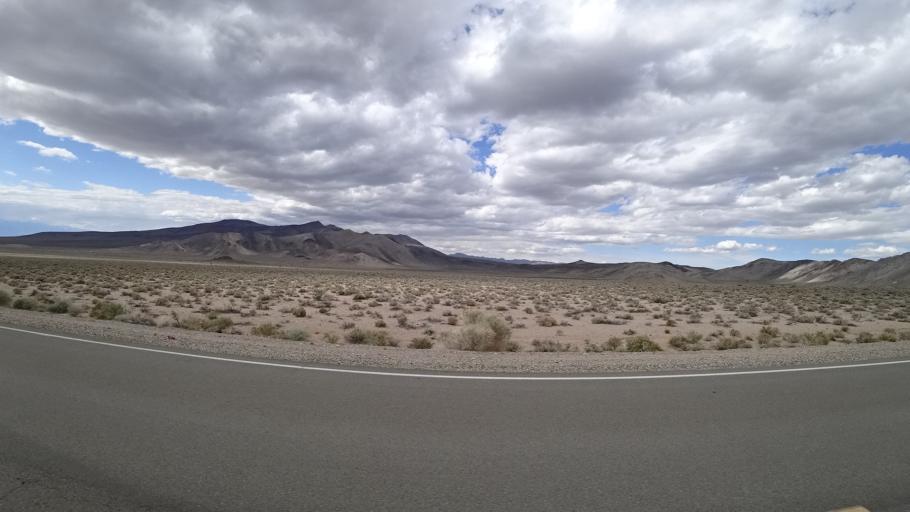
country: US
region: California
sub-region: Inyo County
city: Lone Pine
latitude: 36.3293
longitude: -117.7048
